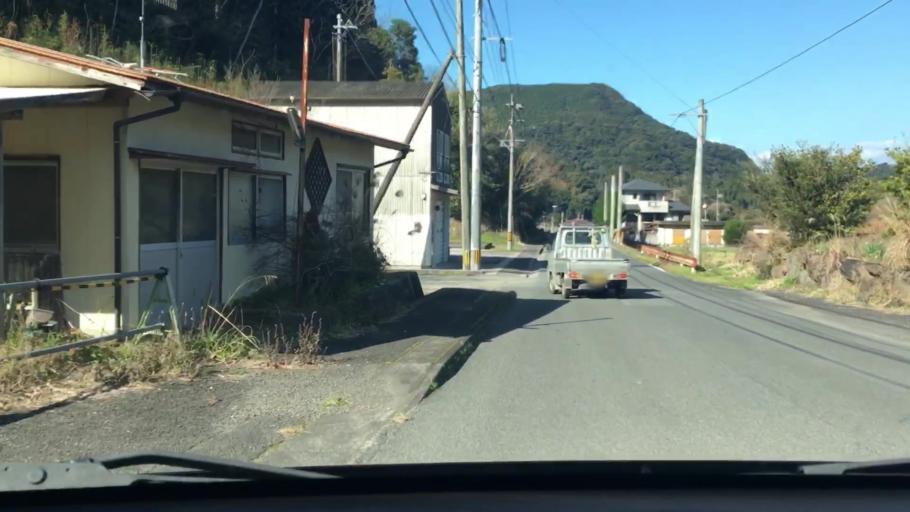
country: JP
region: Kagoshima
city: Ijuin
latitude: 31.7381
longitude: 130.4112
